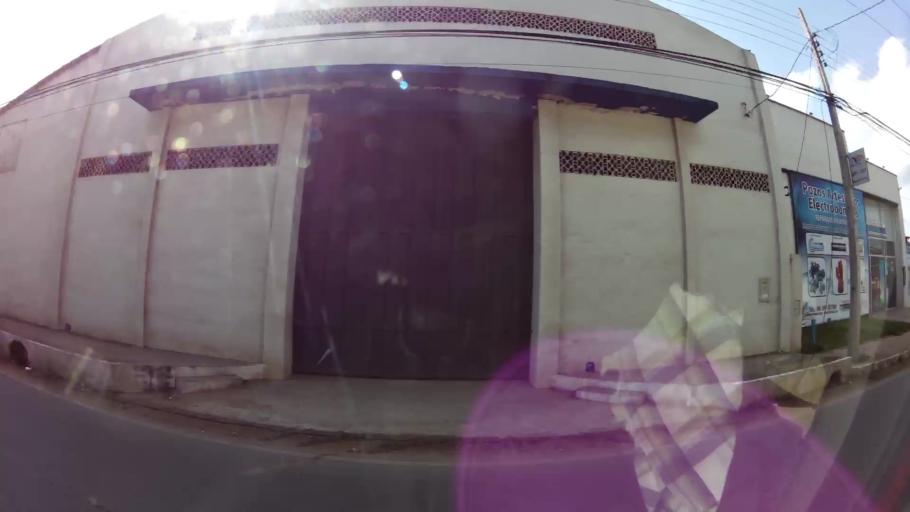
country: PY
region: Central
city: Fernando de la Mora
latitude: -25.3240
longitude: -57.5422
